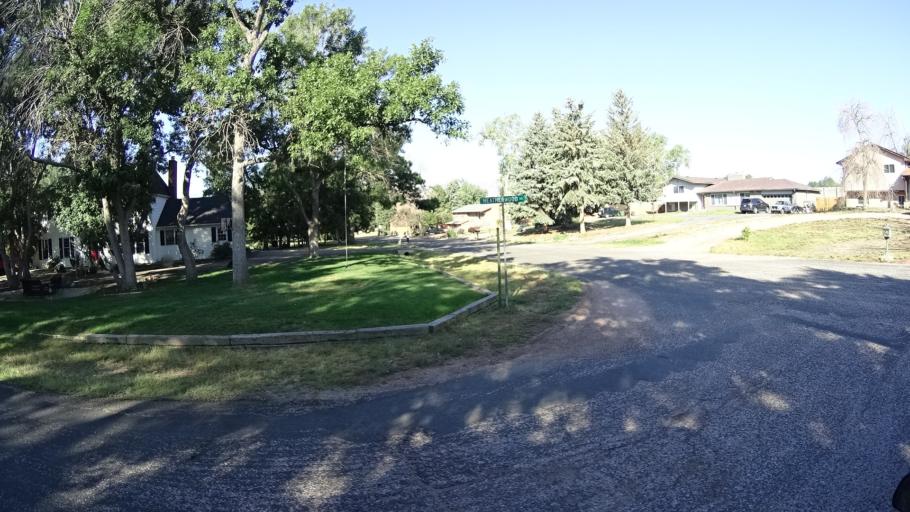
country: US
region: Colorado
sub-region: El Paso County
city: Air Force Academy
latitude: 38.9322
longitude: -104.7854
